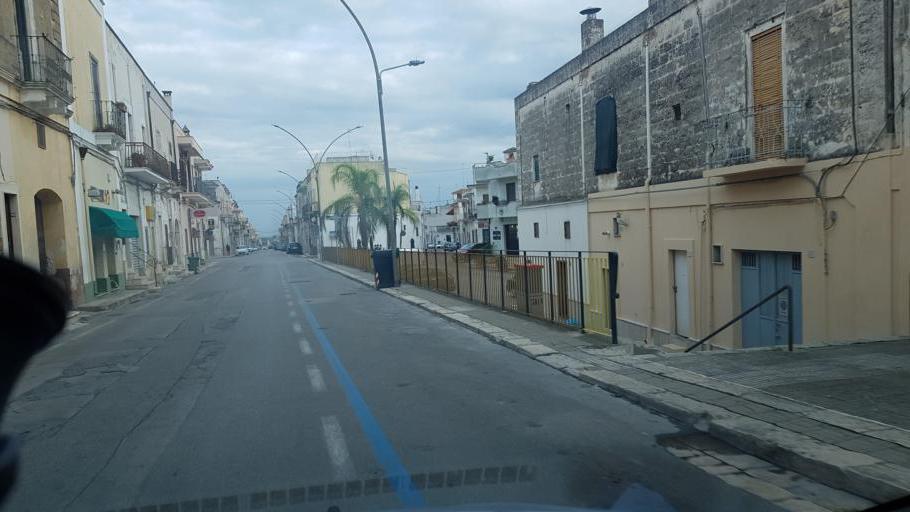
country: IT
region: Apulia
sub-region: Provincia di Brindisi
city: Oria
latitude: 40.4960
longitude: 17.6458
